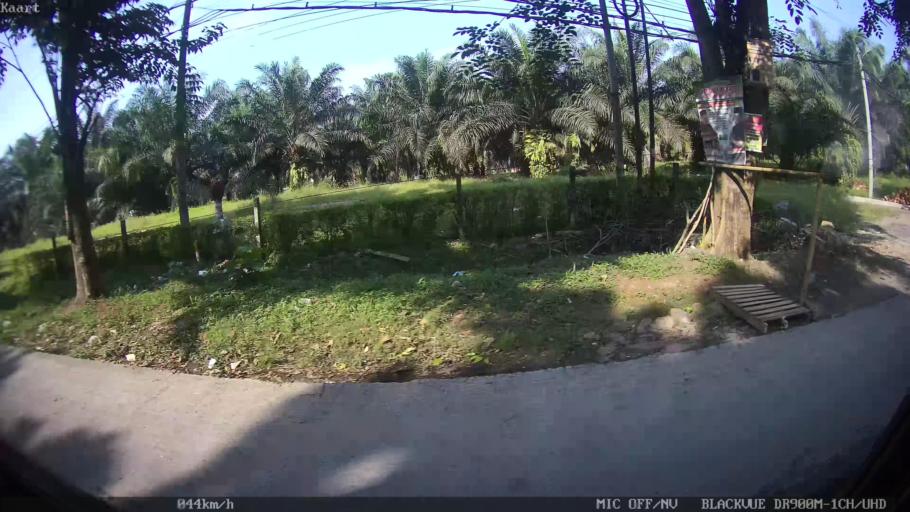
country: ID
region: Lampung
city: Natar
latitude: -5.3307
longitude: 105.2078
